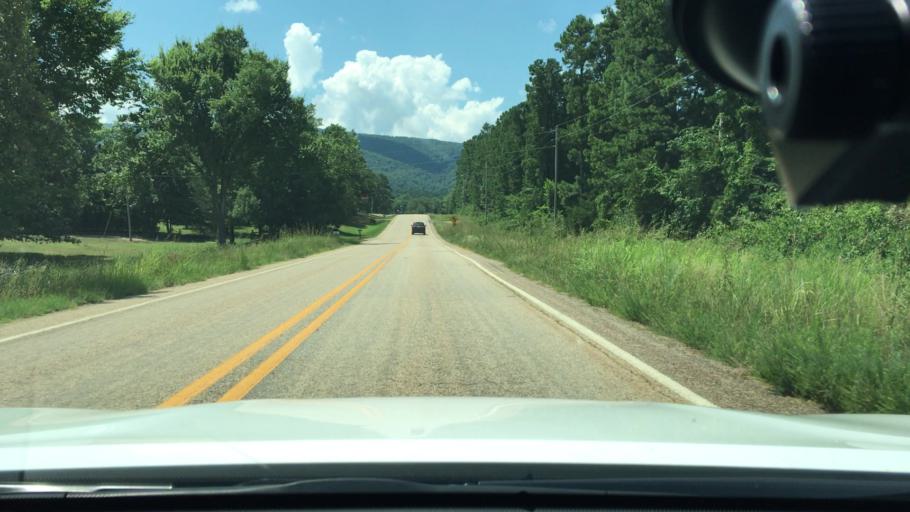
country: US
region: Arkansas
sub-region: Logan County
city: Paris
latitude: 35.2015
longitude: -93.6348
